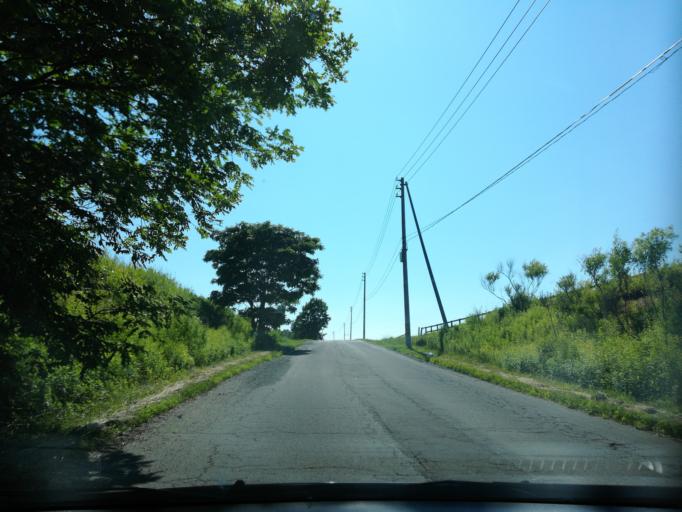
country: JP
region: Hokkaido
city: Chitose
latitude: 42.9220
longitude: 141.8721
